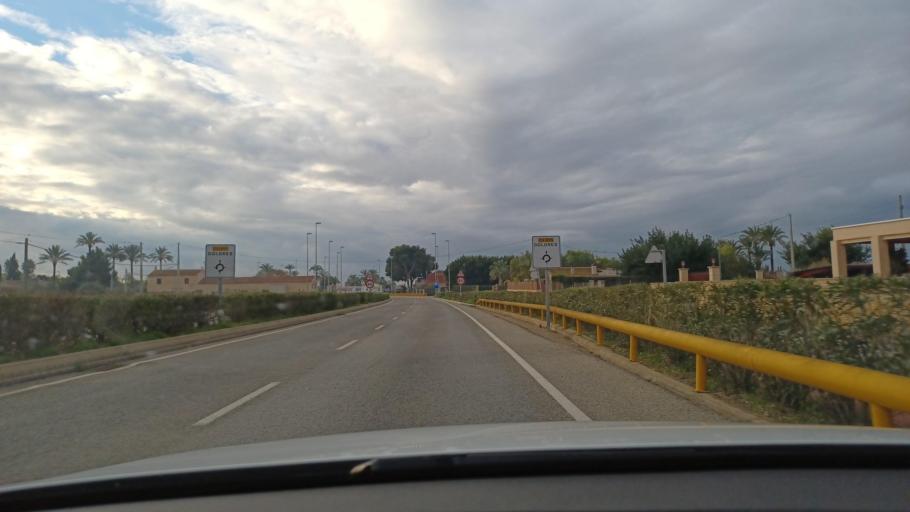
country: ES
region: Valencia
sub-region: Provincia de Alicante
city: Elche
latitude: 38.2167
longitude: -0.6974
